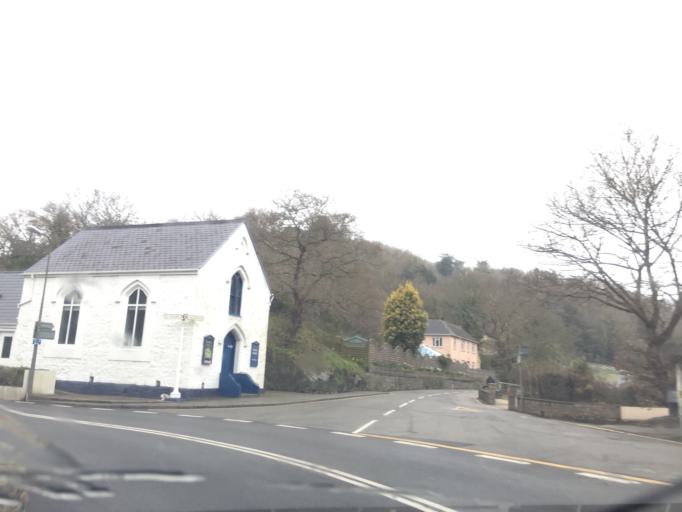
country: JE
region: St Helier
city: Saint Helier
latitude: 49.2048
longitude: -2.1549
